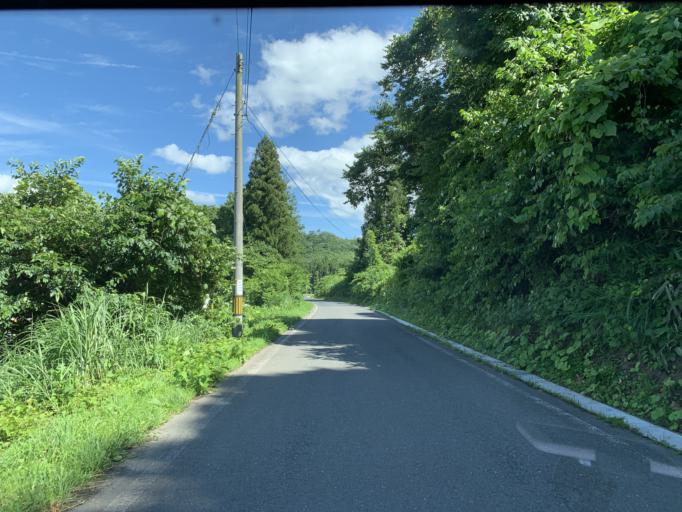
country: JP
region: Iwate
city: Ichinoseki
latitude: 38.9719
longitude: 140.9462
